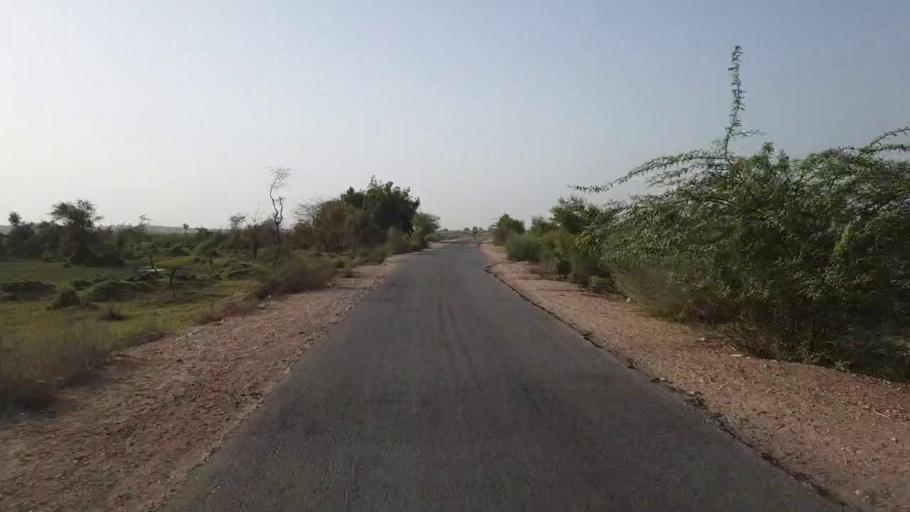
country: PK
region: Sindh
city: Jam Sahib
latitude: 26.4590
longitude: 68.8591
